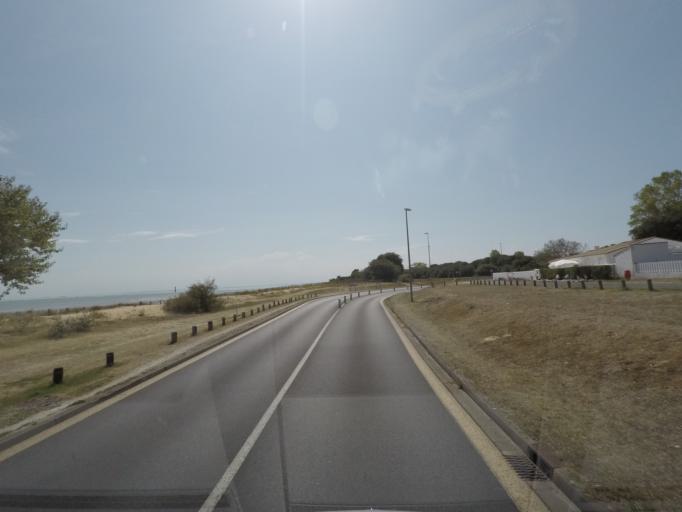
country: FR
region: Poitou-Charentes
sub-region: Departement de la Charente-Maritime
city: Rivedoux-Plage
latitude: 46.1511
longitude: -1.2745
